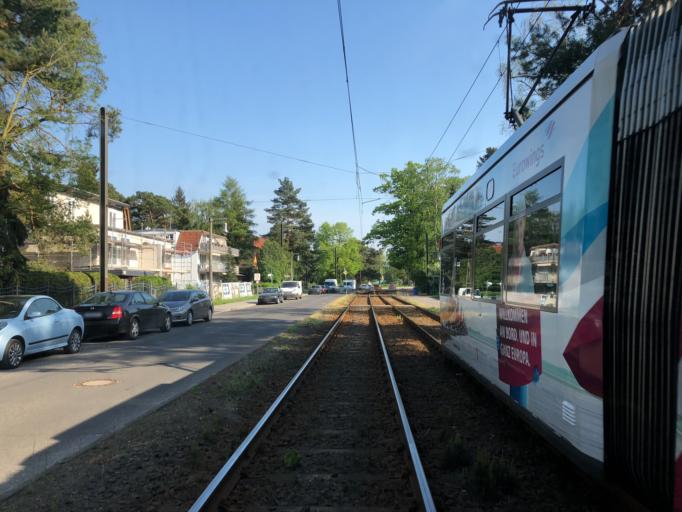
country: DE
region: Berlin
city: Schmockwitz
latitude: 52.3930
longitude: 13.6335
